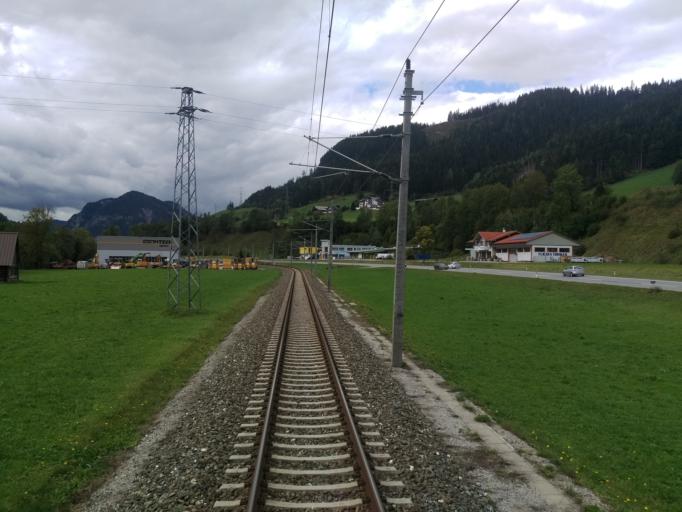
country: AT
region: Styria
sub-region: Politischer Bezirk Liezen
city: Schladming
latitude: 47.3885
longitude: 13.6462
